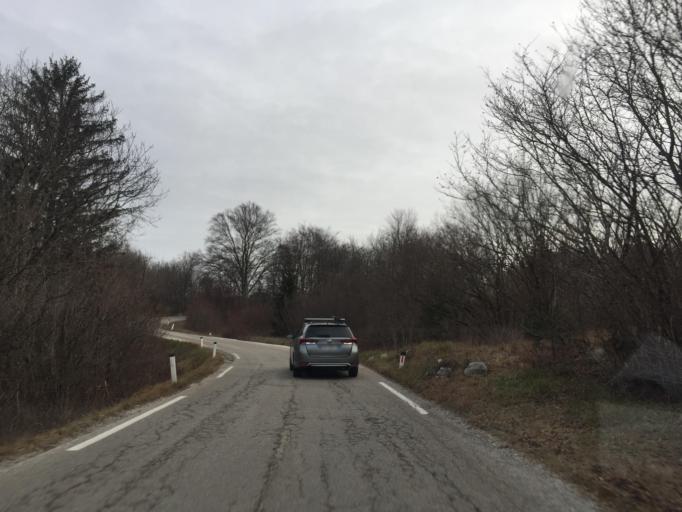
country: SI
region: Nova Gorica
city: Sempas
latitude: 45.9776
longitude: 13.7449
